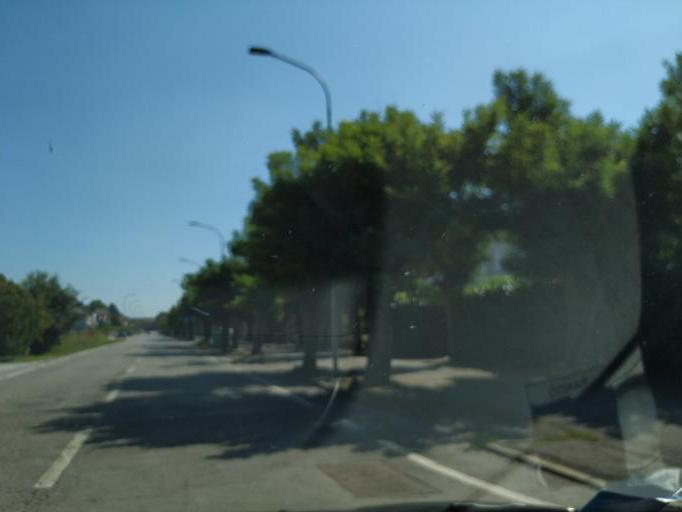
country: IT
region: Emilia-Romagna
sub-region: Provincia di Ferrara
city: Coccanile-Cesta
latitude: 44.9123
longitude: 11.9059
